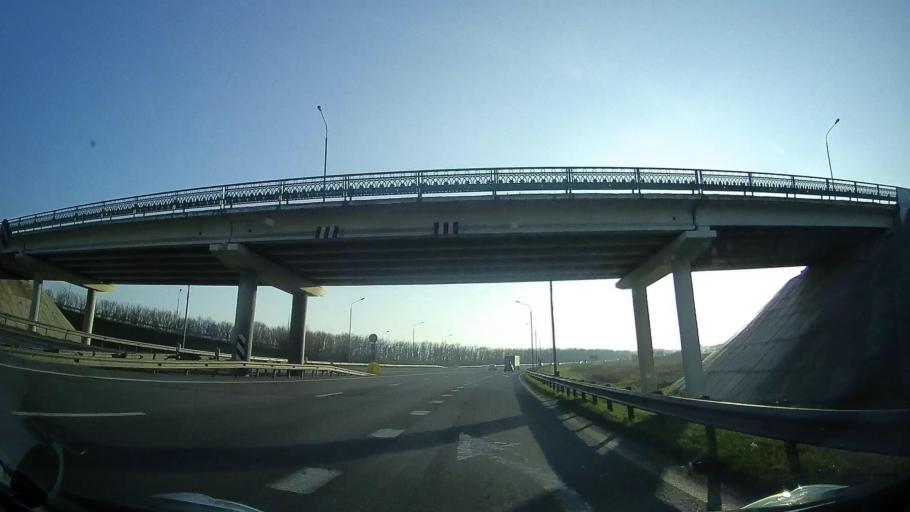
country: RU
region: Rostov
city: Ol'ginskaya
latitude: 47.1288
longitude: 39.8754
